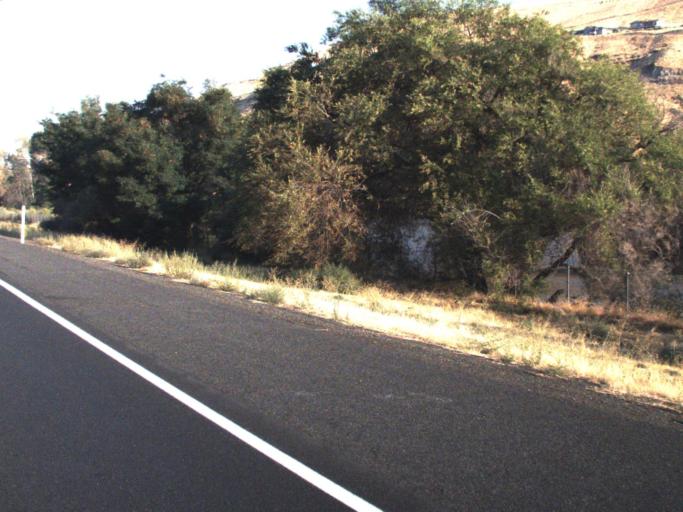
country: US
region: Washington
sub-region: Yakima County
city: Yakima
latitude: 46.6274
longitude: -120.5097
